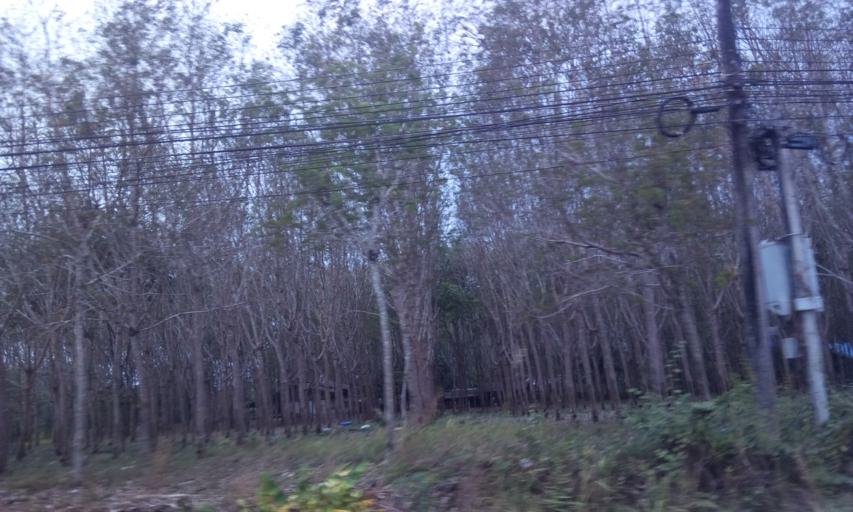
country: TH
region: Trat
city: Khao Saming
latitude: 12.2885
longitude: 102.3154
